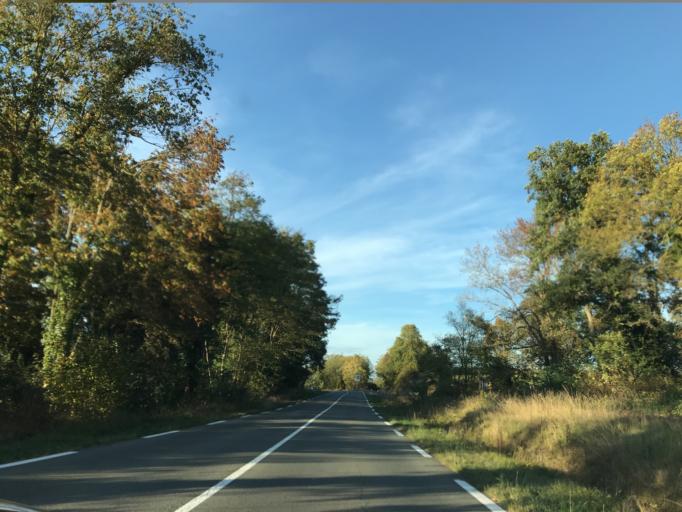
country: FR
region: Auvergne
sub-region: Departement du Puy-de-Dome
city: Puy-Guillaume
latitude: 45.9705
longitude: 3.4797
